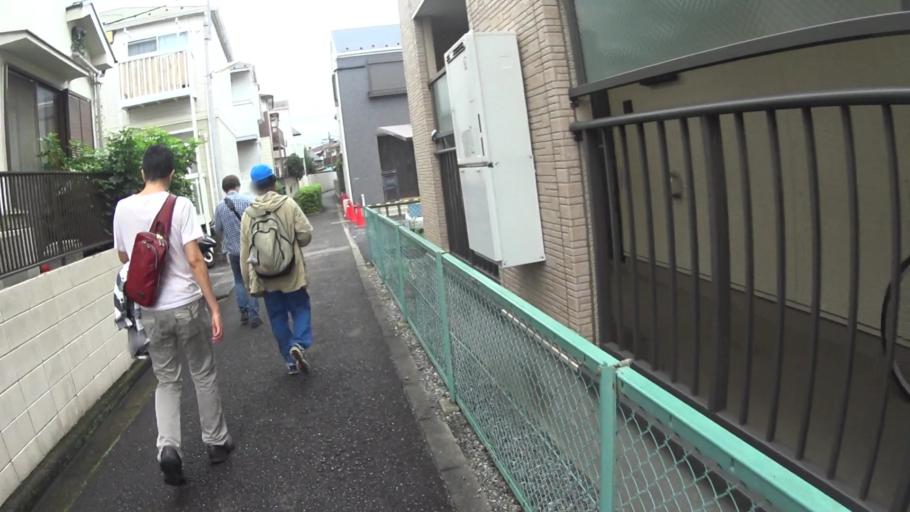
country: JP
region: Tokyo
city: Tokyo
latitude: 35.7381
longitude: 139.6805
